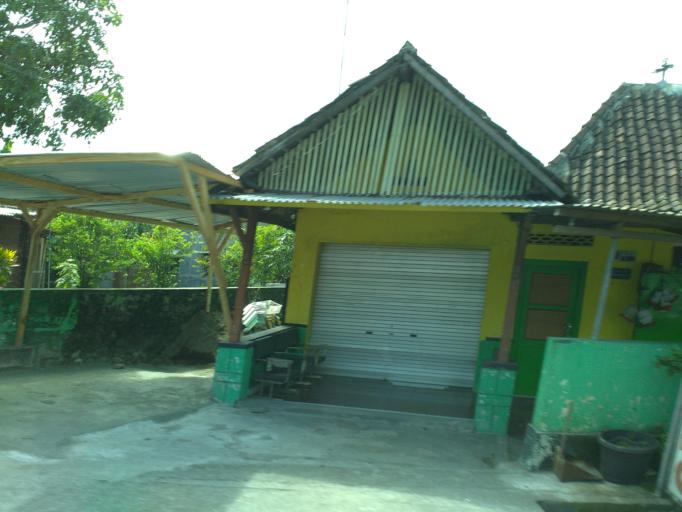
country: ID
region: Central Java
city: Candi Prambanan
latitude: -7.7452
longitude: 110.5270
